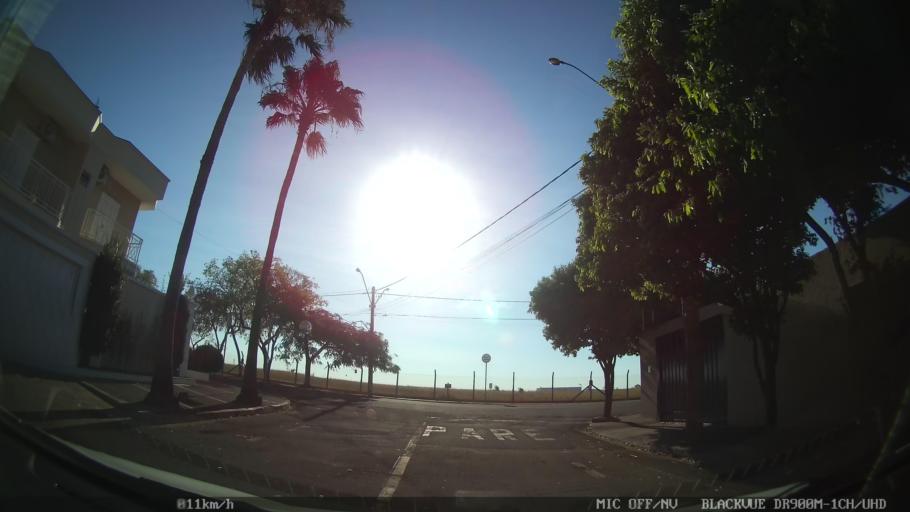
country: BR
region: Sao Paulo
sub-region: Sao Jose Do Rio Preto
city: Sao Jose do Rio Preto
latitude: -20.8215
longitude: -49.4109
